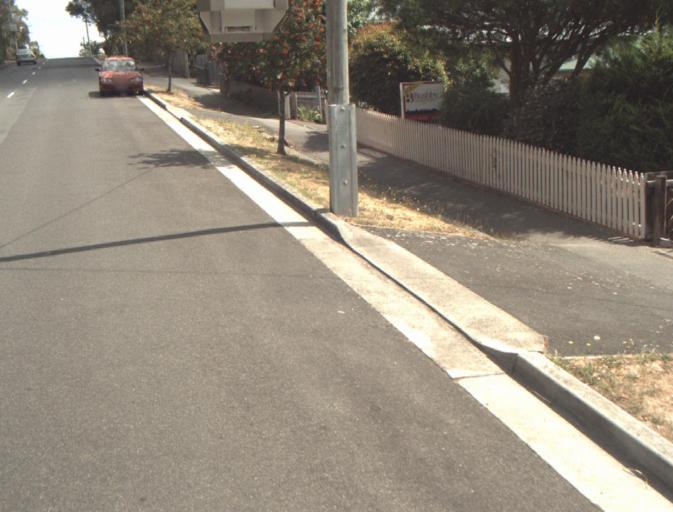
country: AU
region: Tasmania
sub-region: Launceston
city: Newstead
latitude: -41.4668
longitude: 147.1761
